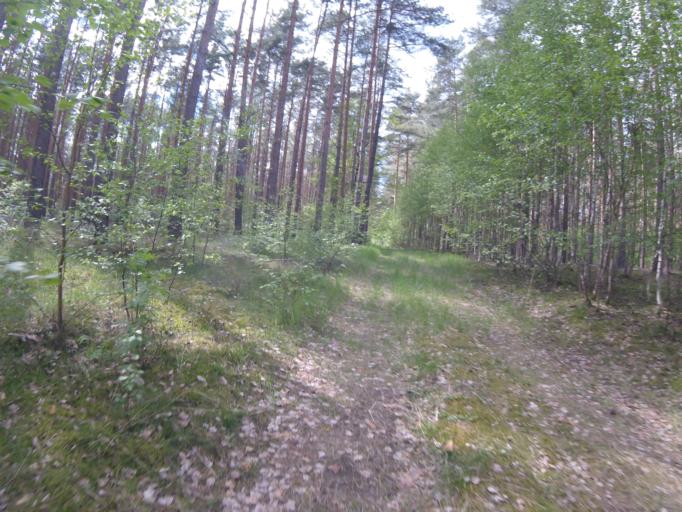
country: DE
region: Brandenburg
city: Teupitz
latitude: 52.1540
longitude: 13.6012
